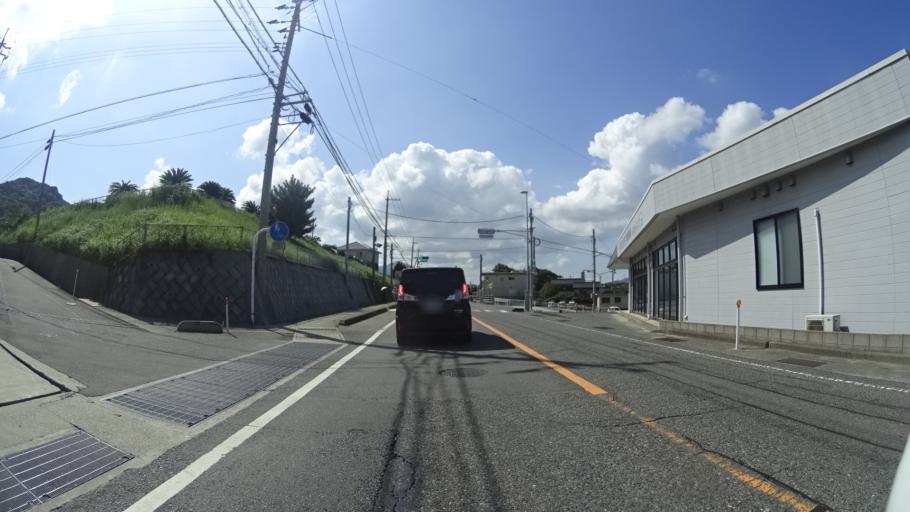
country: JP
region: Yamaguchi
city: Shimonoseki
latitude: 34.1641
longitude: 130.9270
